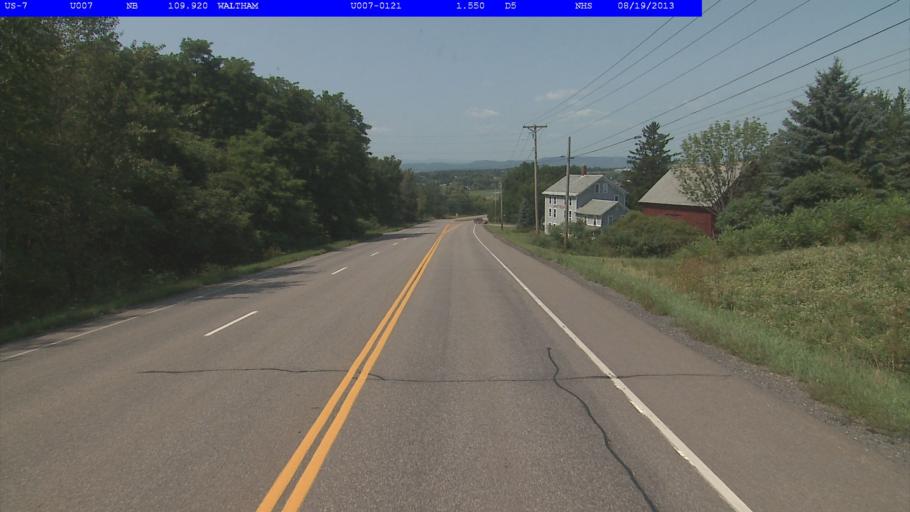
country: US
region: Vermont
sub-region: Addison County
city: Vergennes
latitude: 44.1623
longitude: -73.2334
